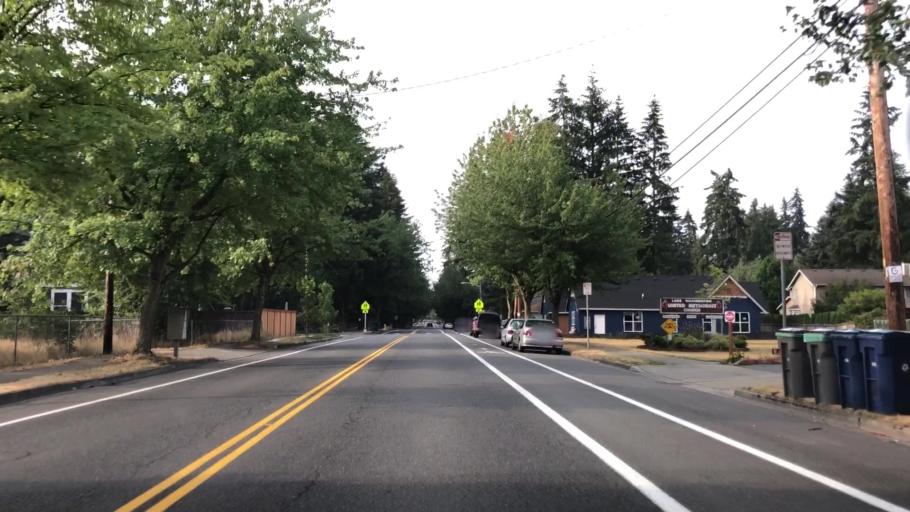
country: US
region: Washington
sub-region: King County
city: Redmond
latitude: 47.6725
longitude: -122.1639
